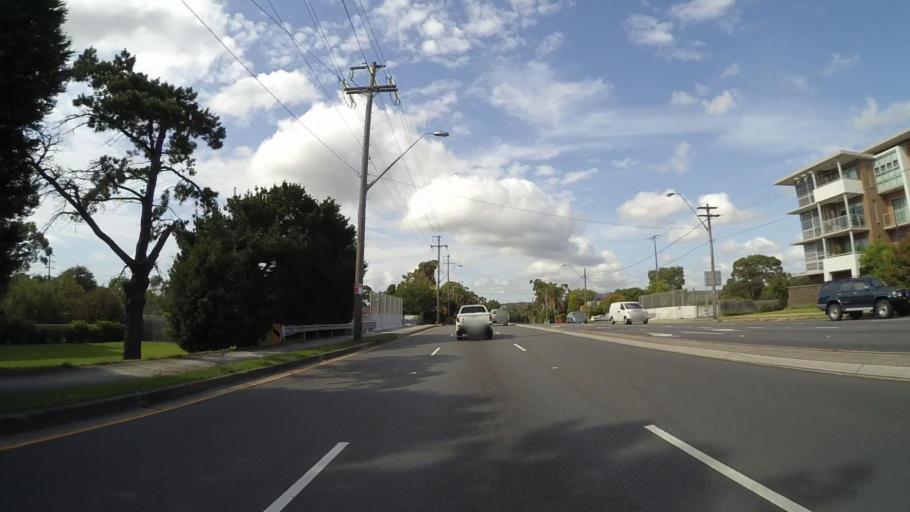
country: AU
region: New South Wales
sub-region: Sutherland Shire
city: Kirrawee
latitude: -34.0354
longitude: 151.0662
